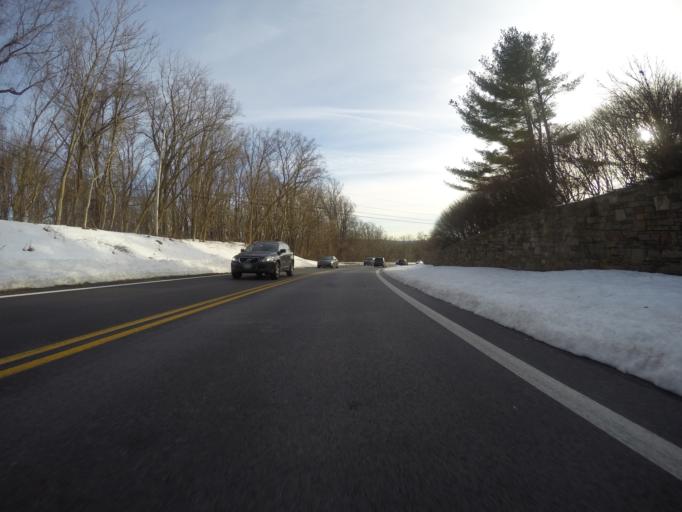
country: US
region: Maryland
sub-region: Baltimore County
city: Hampton
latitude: 39.4671
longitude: -76.5746
